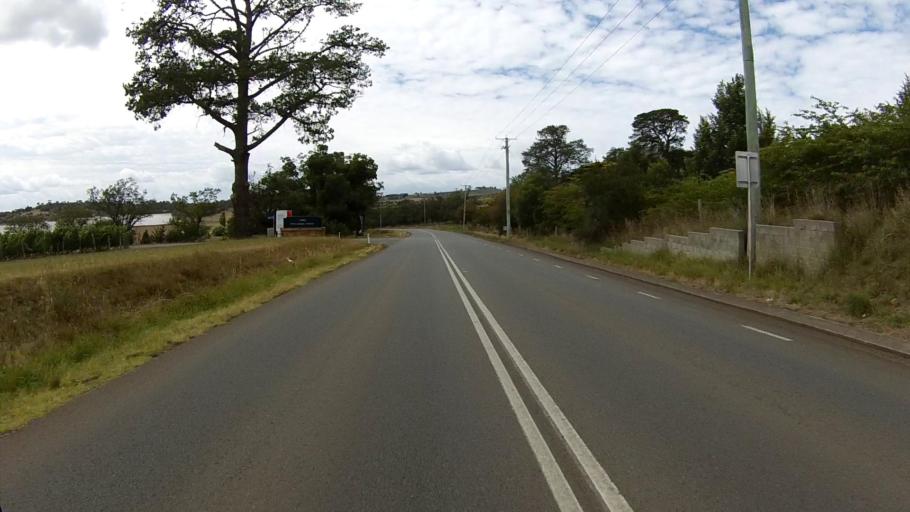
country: AU
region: Tasmania
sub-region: Clarence
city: Cambridge
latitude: -42.8095
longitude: 147.4267
